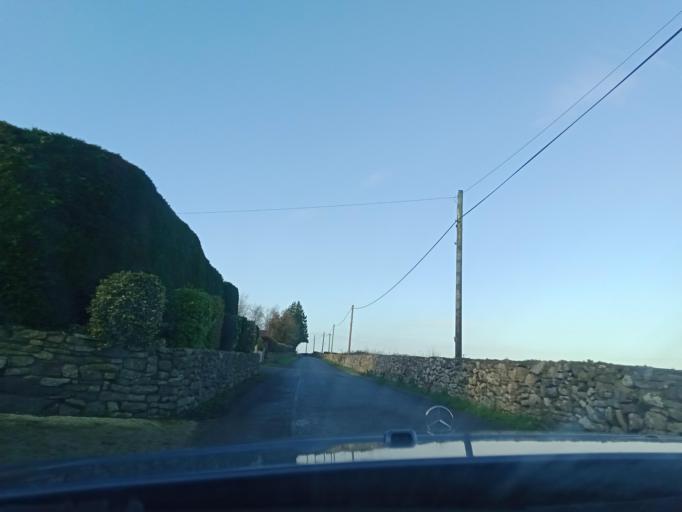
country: IE
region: Leinster
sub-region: Kilkenny
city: Callan
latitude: 52.4711
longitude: -7.4184
